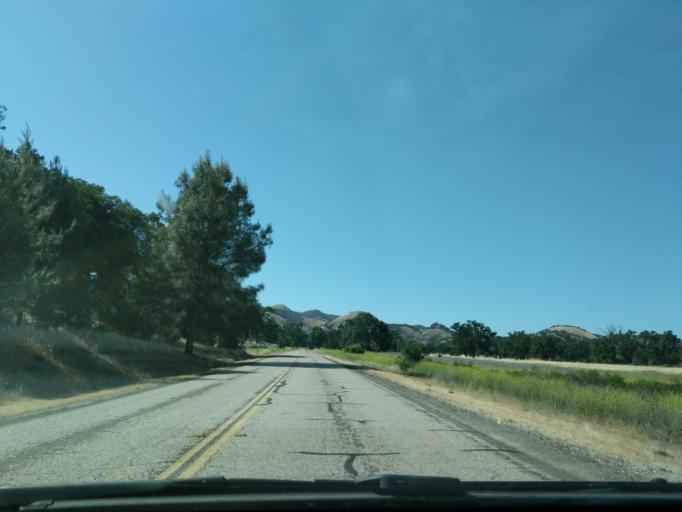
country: US
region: California
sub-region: Monterey County
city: King City
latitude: 36.0346
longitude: -121.1786
